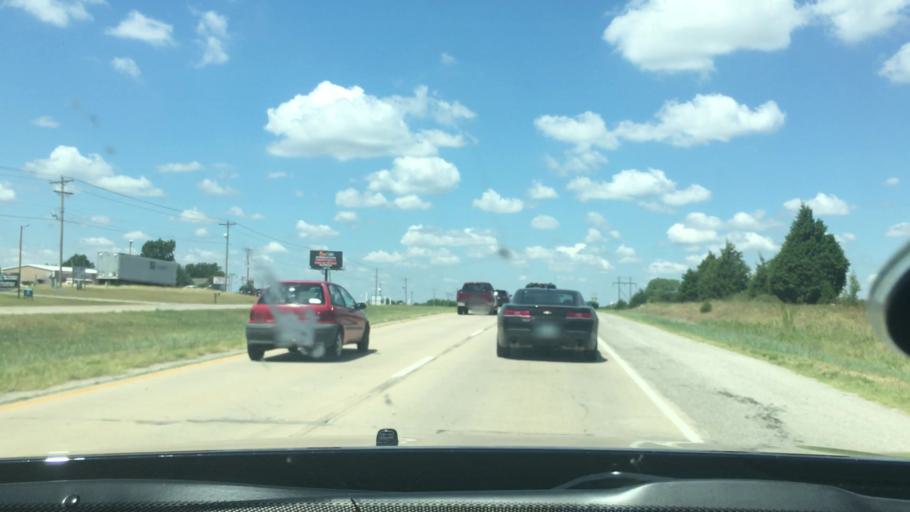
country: US
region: Oklahoma
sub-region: Carter County
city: Lone Grove
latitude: 34.1730
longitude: -97.2175
